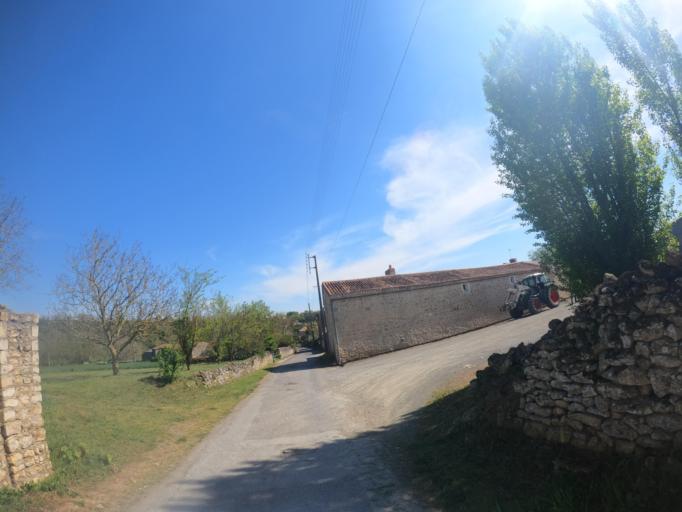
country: FR
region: Poitou-Charentes
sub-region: Departement des Deux-Sevres
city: Airvault
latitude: 46.8864
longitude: -0.1419
